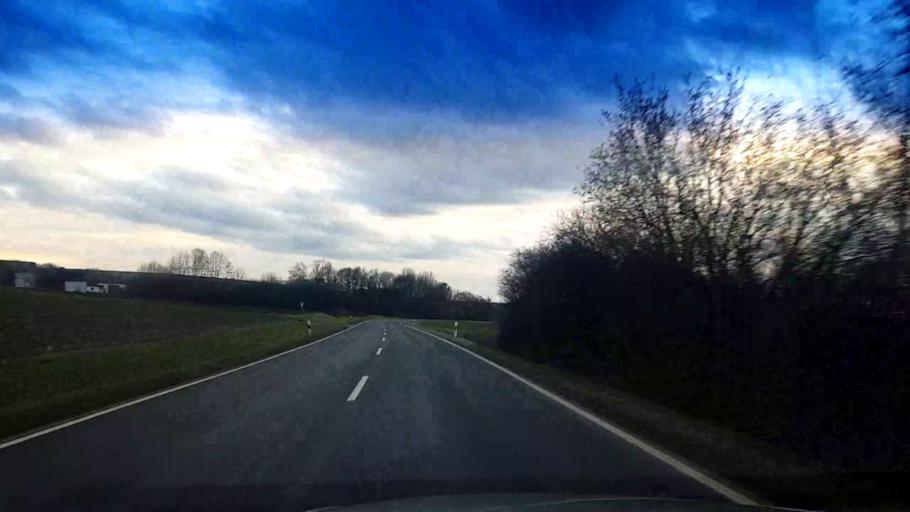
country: DE
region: Bavaria
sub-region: Upper Franconia
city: Strullendorf
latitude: 49.8627
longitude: 11.0171
